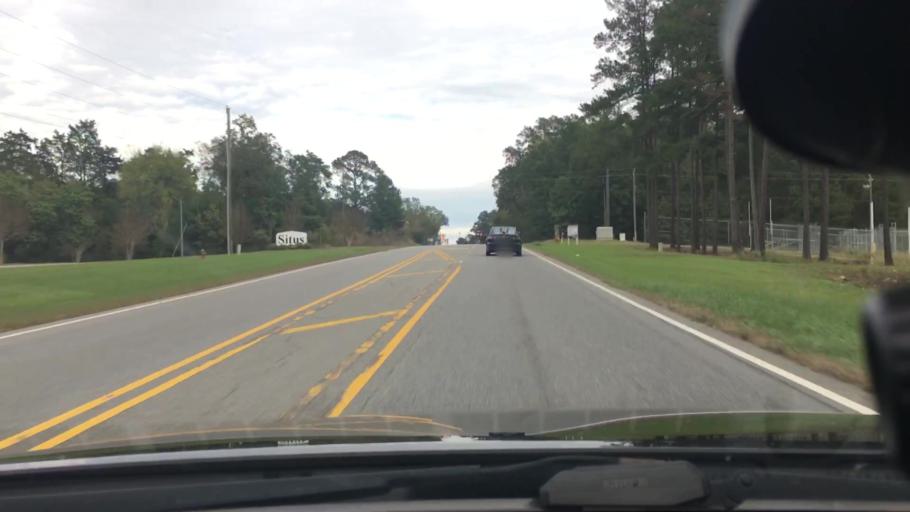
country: US
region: North Carolina
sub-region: Moore County
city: Robbins
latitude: 35.4044
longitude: -79.5787
